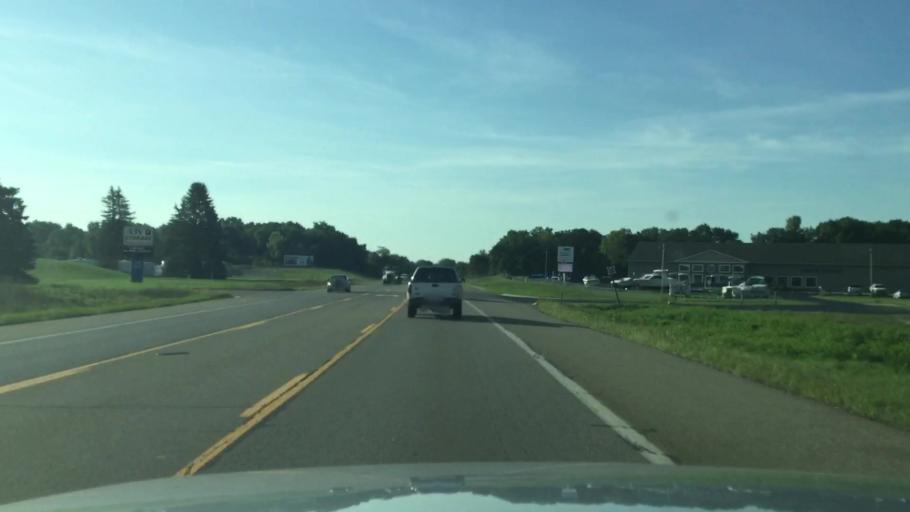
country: US
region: Michigan
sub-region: Jackson County
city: Vandercook Lake
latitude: 42.1855
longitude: -84.3684
